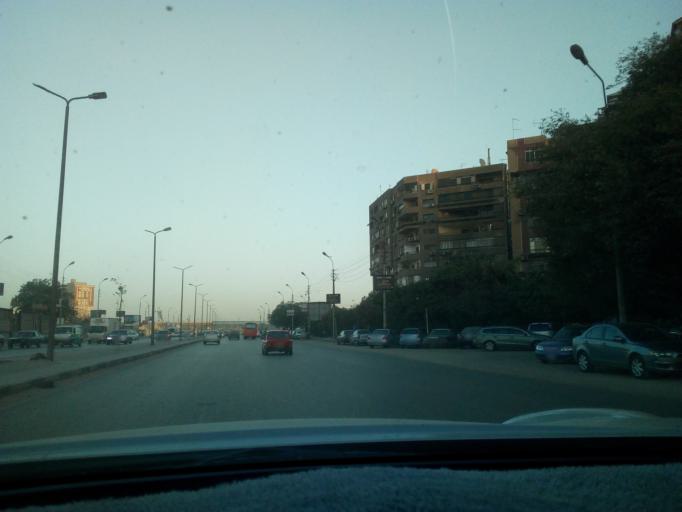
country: EG
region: Muhafazat al Qalyubiyah
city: Al Khankah
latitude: 30.1175
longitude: 31.3610
